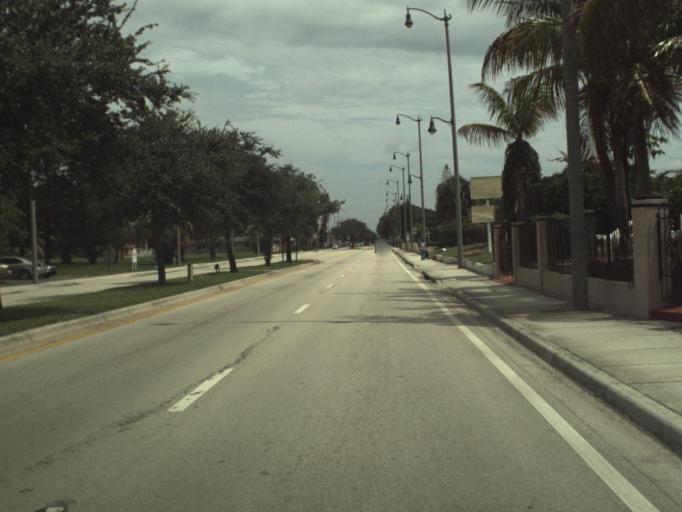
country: US
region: Florida
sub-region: Palm Beach County
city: West Palm Beach
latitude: 26.7372
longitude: -80.0567
